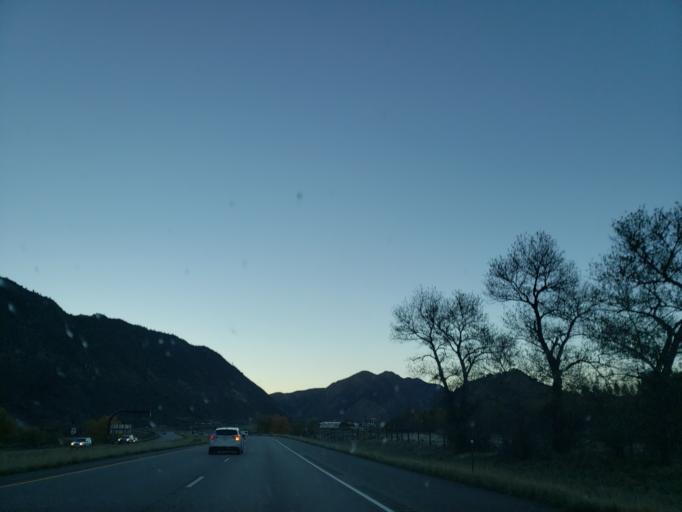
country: US
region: Colorado
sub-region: Garfield County
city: New Castle
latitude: 39.5663
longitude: -107.5076
